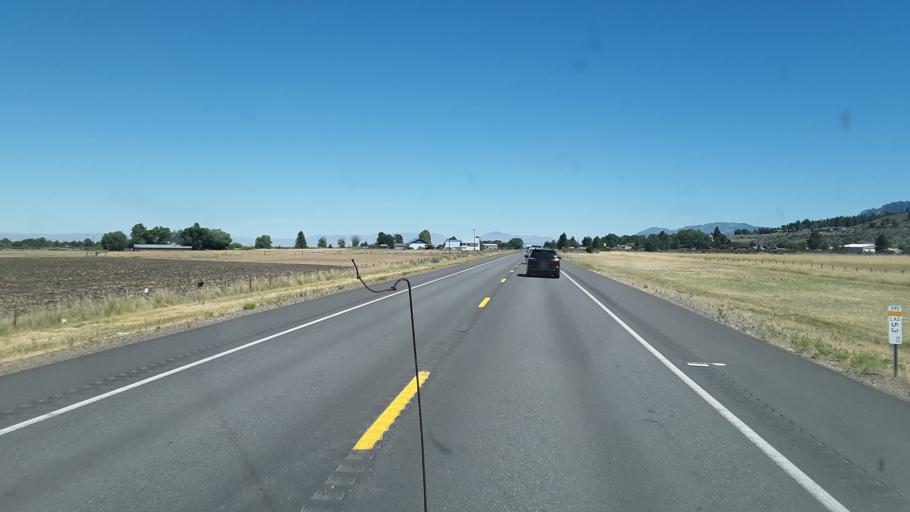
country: US
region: California
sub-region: Lassen County
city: Janesville
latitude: 40.2980
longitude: -120.5149
